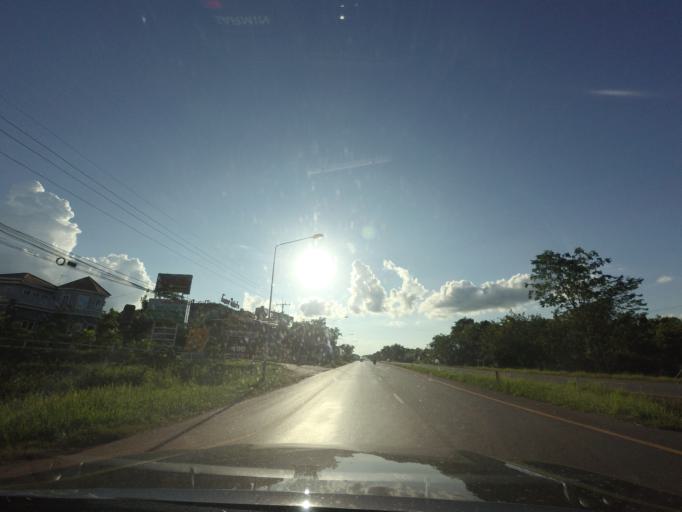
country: TH
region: Changwat Udon Thani
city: Nong Han
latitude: 17.3637
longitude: 103.0624
